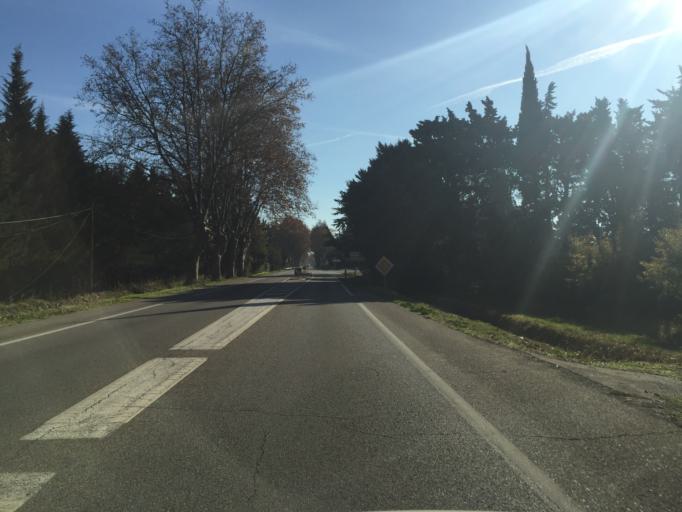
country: FR
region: Provence-Alpes-Cote d'Azur
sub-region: Departement des Bouches-du-Rhone
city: Orgon
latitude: 43.7724
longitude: 5.0566
